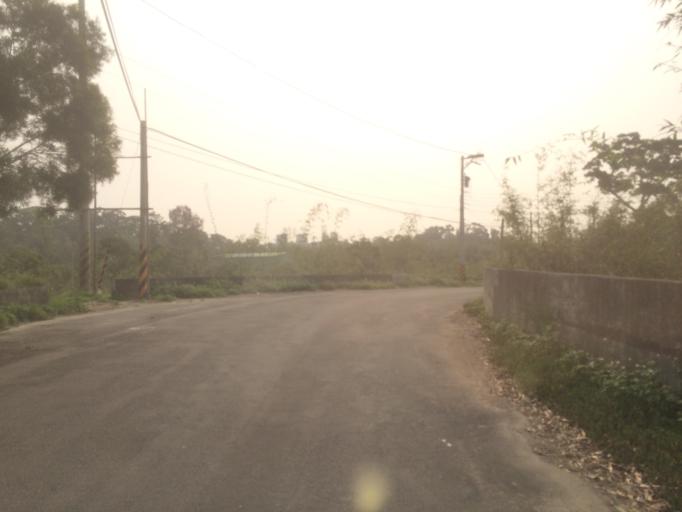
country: TW
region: Taiwan
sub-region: Hsinchu
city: Hsinchu
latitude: 24.7645
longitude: 120.9720
